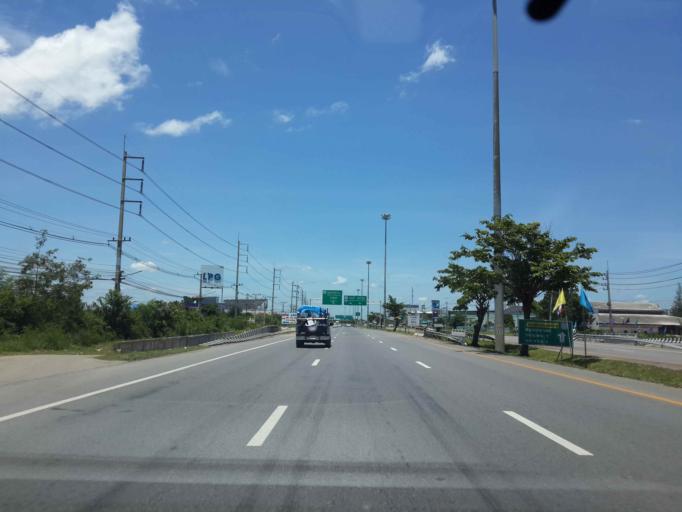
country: TH
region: Ratchaburi
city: Pak Tho
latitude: 13.3289
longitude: 99.8291
